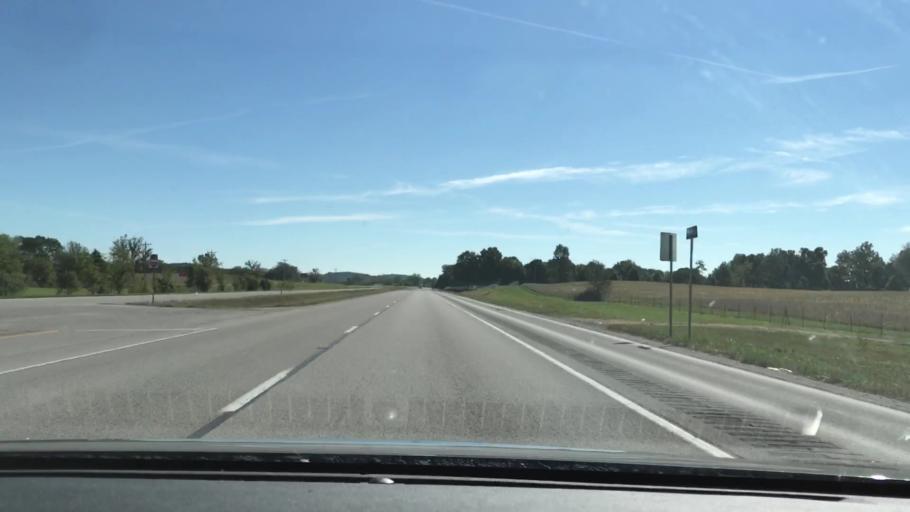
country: US
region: Kentucky
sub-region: Todd County
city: Elkton
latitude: 36.8437
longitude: -87.2699
